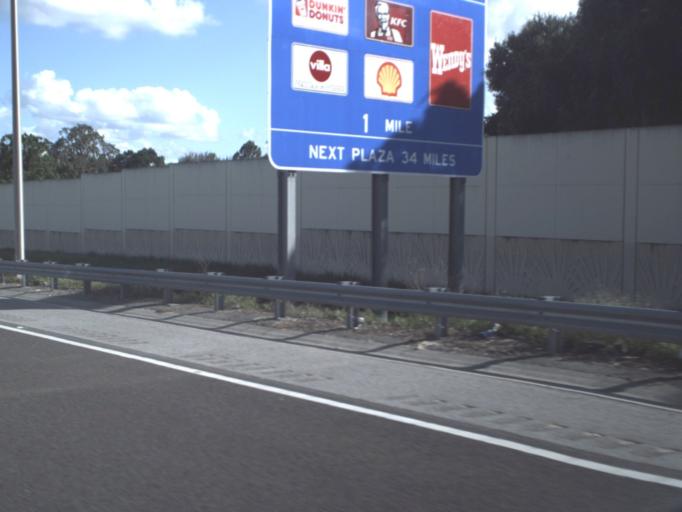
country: US
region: Florida
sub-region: Orange County
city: Gotha
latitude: 28.5300
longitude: -81.5212
